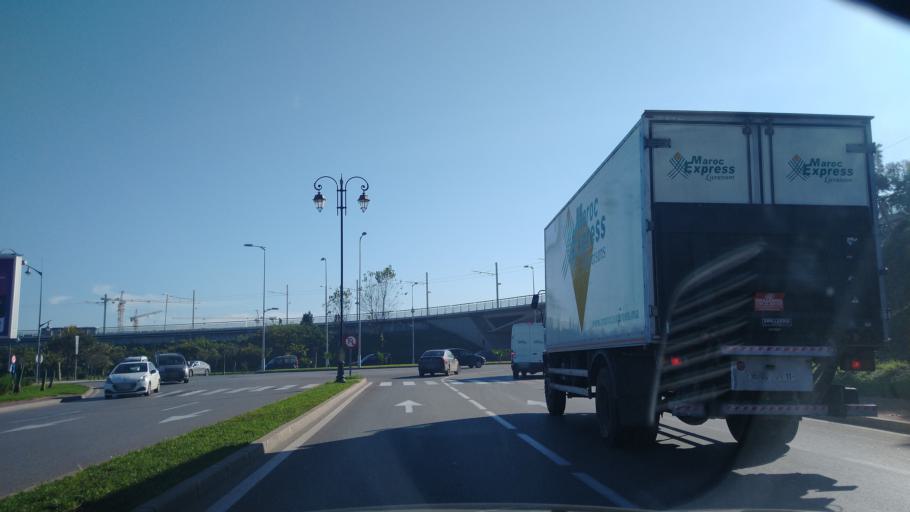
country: MA
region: Rabat-Sale-Zemmour-Zaer
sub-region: Rabat
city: Rabat
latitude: 34.0255
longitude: -6.8216
